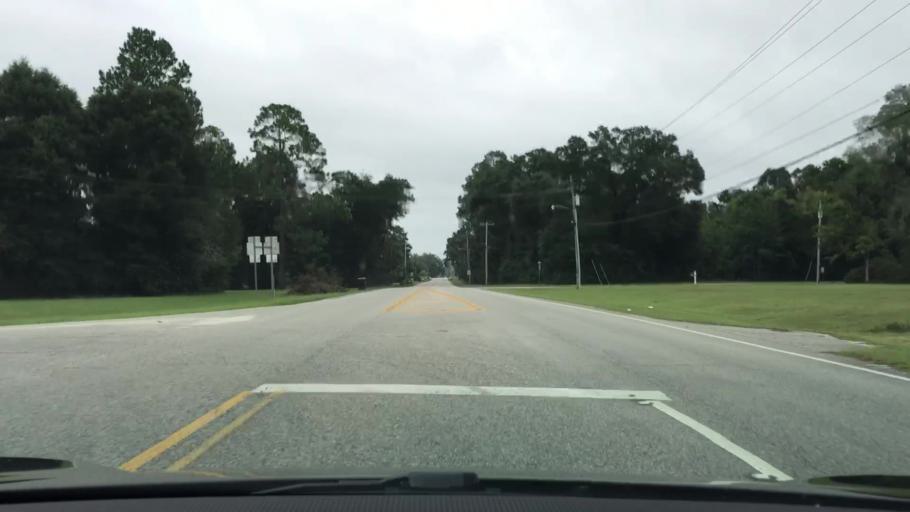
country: US
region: Alabama
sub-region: Coffee County
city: Elba
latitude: 31.4050
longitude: -86.0810
